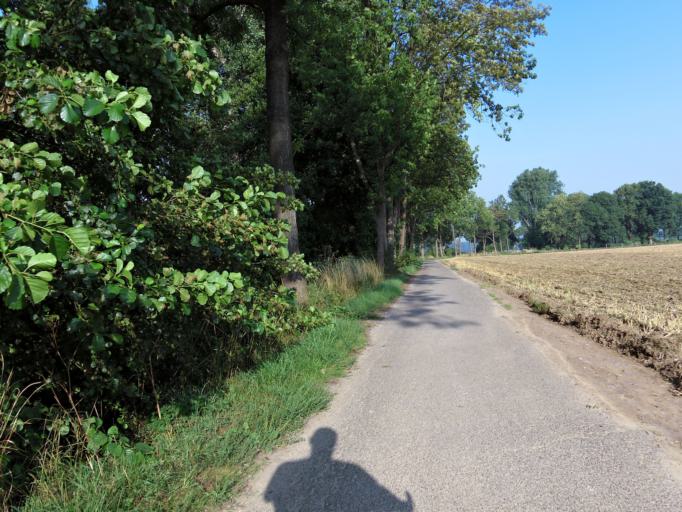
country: DE
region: North Rhine-Westphalia
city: Huckelhoven
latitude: 51.0142
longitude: 6.2261
